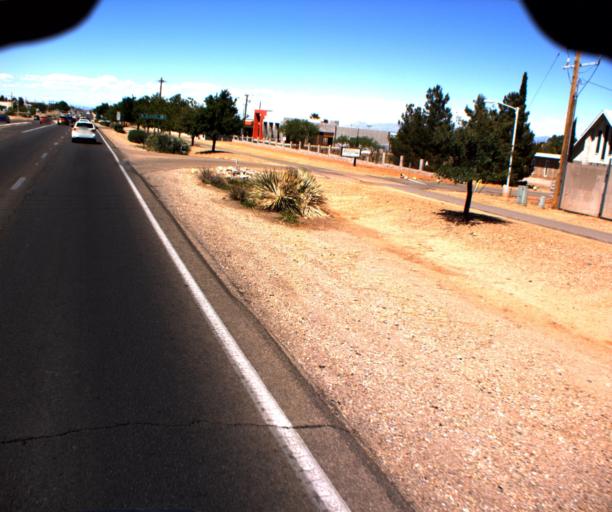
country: US
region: Arizona
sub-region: Cochise County
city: Sierra Vista
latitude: 31.5462
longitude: -110.2573
